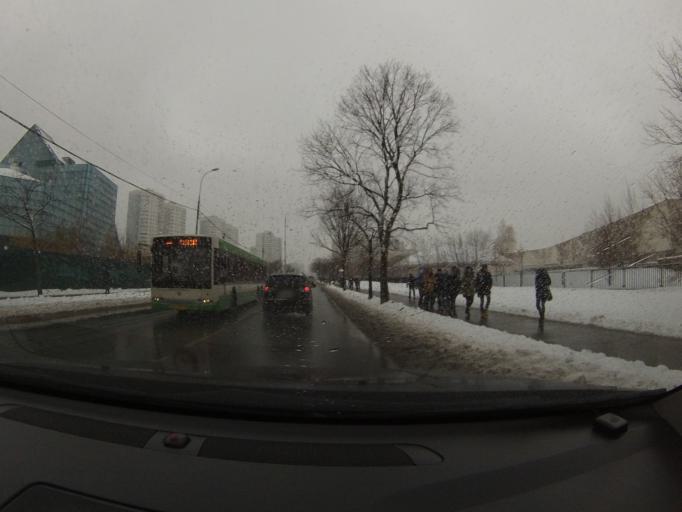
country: RU
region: Moscow
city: Troparevo
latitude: 55.6679
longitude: 37.4800
